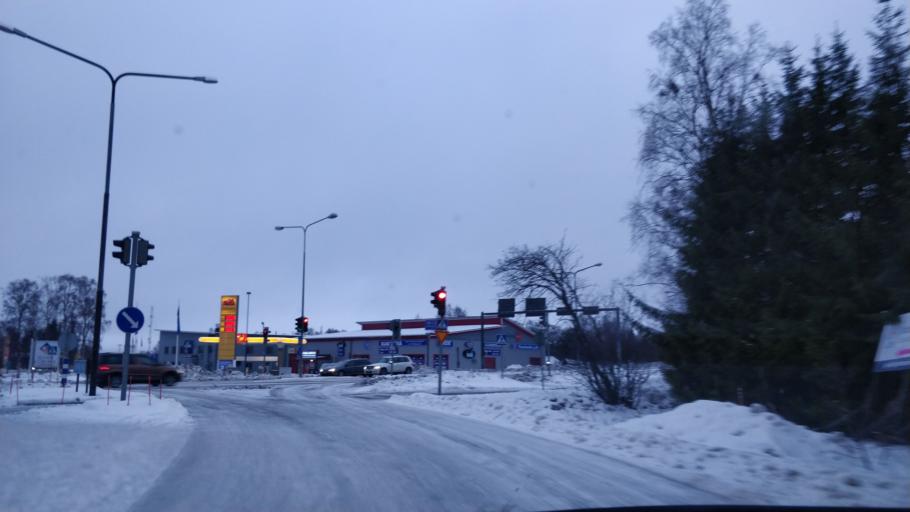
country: FI
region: Lapland
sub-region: Kemi-Tornio
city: Kemi
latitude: 65.7433
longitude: 24.5755
